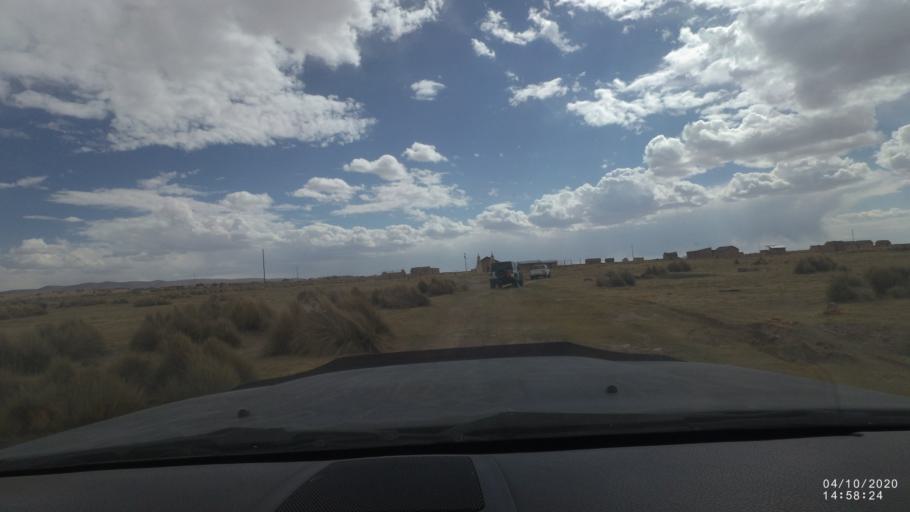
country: BO
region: Oruro
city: Poopo
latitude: -18.6863
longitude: -67.5212
